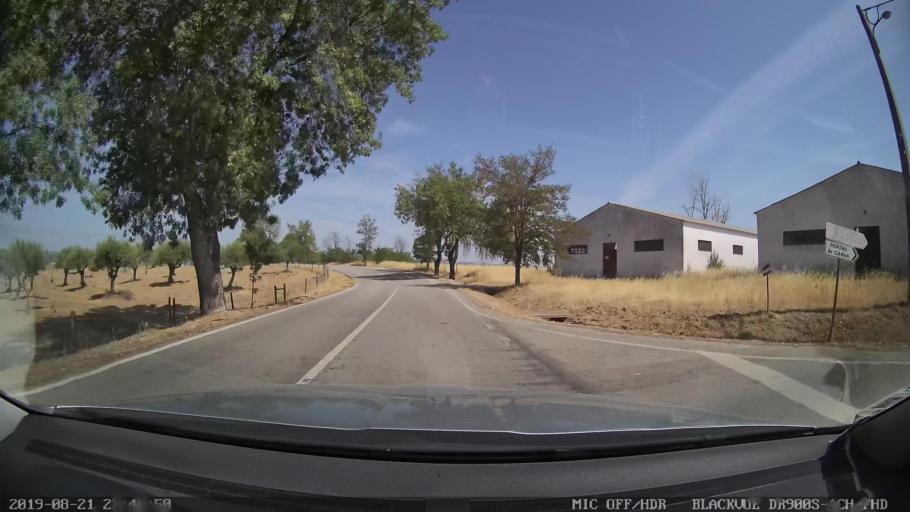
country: PT
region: Castelo Branco
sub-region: Idanha-A-Nova
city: Idanha-a-Nova
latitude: 39.8448
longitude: -7.2564
